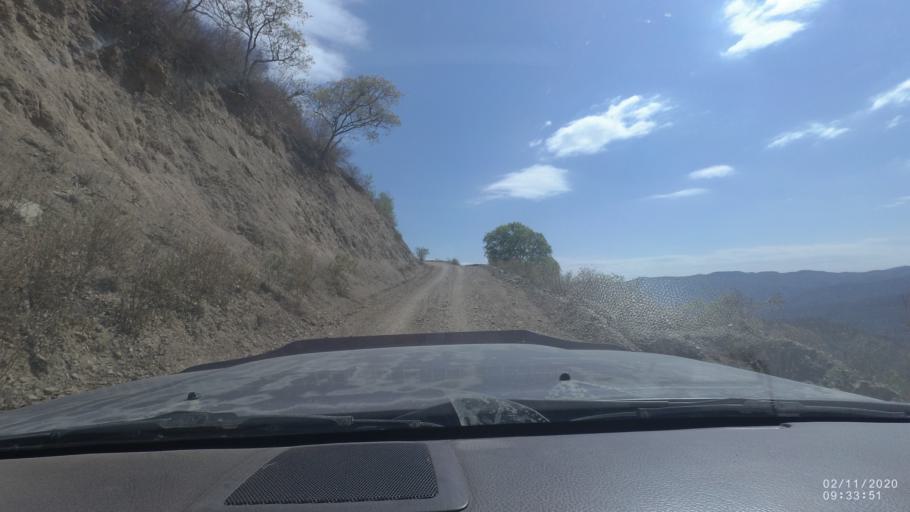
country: BO
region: Chuquisaca
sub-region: Provincia Zudanez
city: Mojocoya
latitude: -18.4102
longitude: -64.5866
